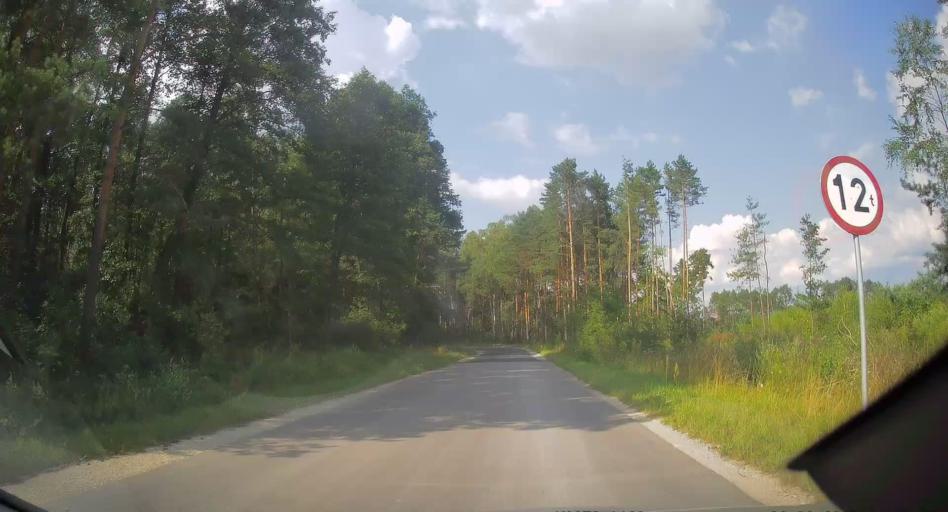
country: PL
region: Swietokrzyskie
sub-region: Powiat konecki
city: Radoszyce
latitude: 51.1022
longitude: 20.2654
